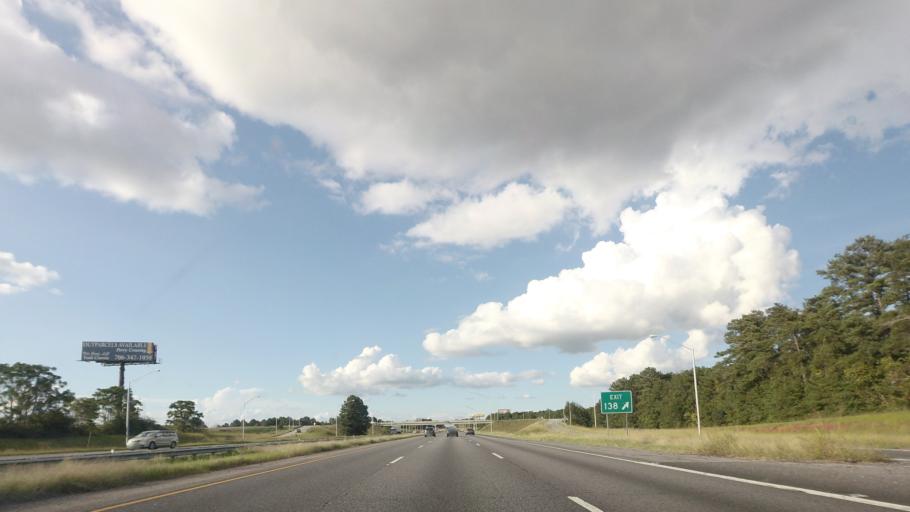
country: US
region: Georgia
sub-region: Houston County
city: Perry
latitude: 32.4904
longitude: -83.7425
